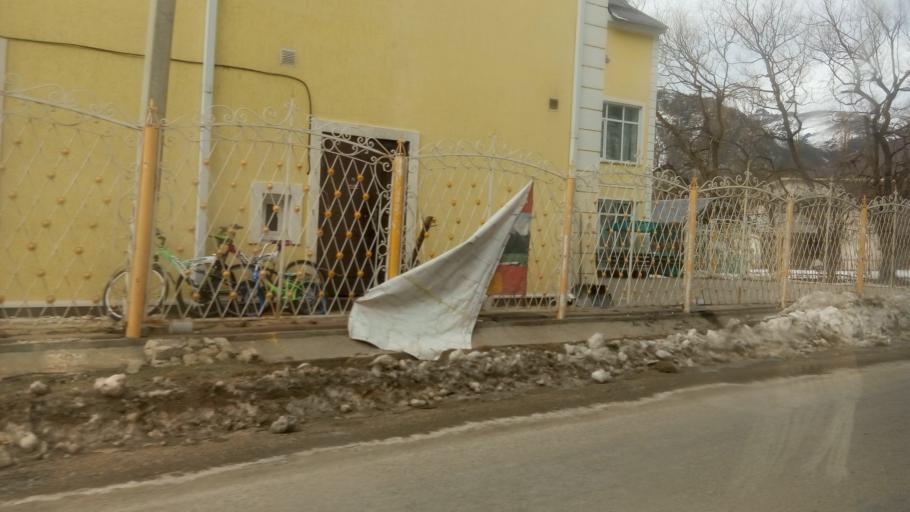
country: RU
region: Karachayevo-Cherkesiya
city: Teberda
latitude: 43.4306
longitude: 41.7428
